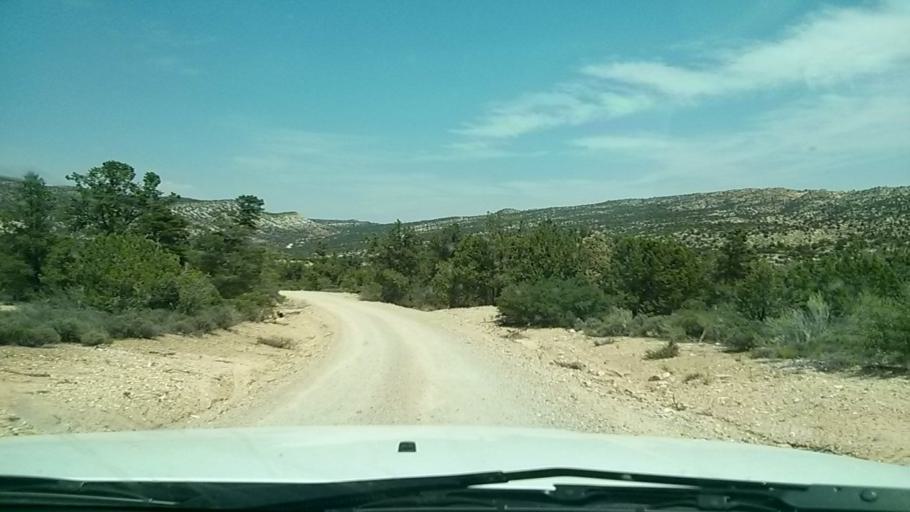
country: US
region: Utah
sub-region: Washington County
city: Washington
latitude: 37.2527
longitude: -113.4309
